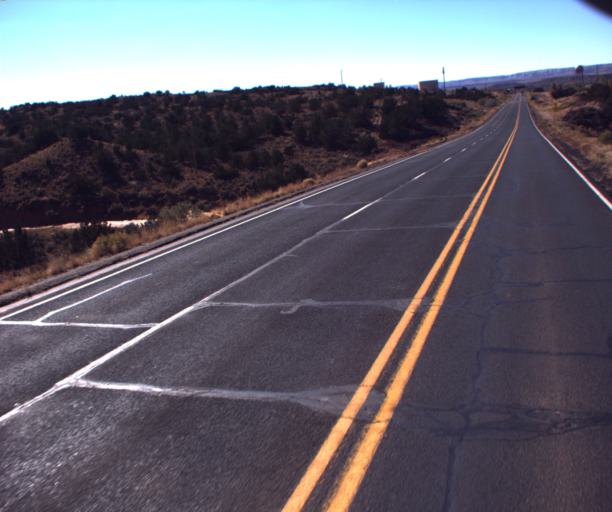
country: US
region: Arizona
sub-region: Apache County
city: Ganado
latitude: 35.7101
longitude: -109.5245
